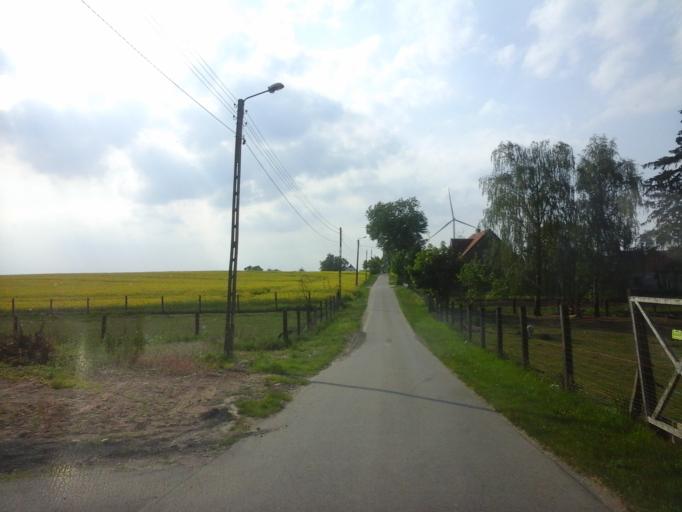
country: PL
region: West Pomeranian Voivodeship
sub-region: Powiat choszczenski
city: Pelczyce
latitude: 53.0309
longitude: 15.2730
